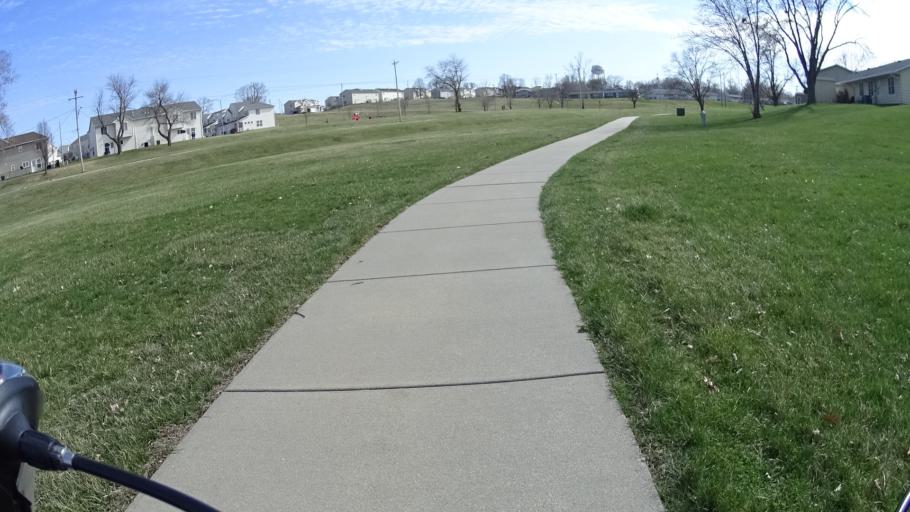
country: US
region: Nebraska
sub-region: Sarpy County
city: Offutt Air Force Base
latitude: 41.1275
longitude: -95.9543
